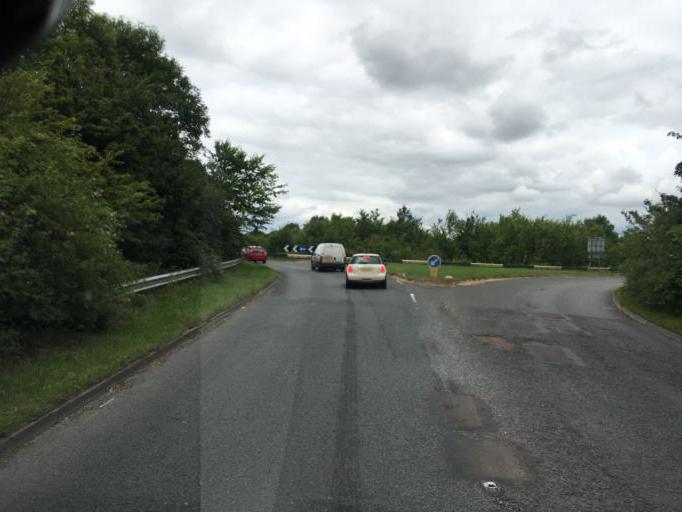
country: GB
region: England
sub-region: Gloucestershire
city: Stonehouse
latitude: 51.7587
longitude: -2.3211
